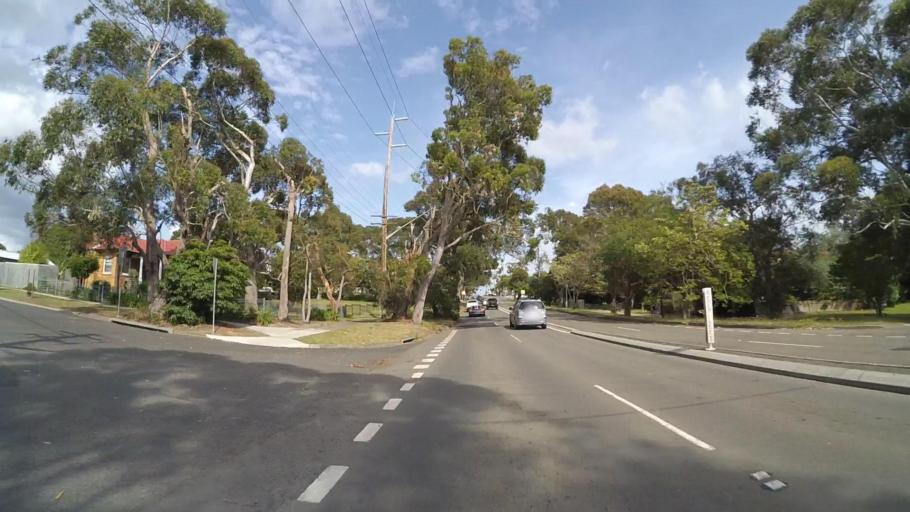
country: AU
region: New South Wales
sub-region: Sutherland Shire
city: Gymea
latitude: -34.0381
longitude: 151.0870
